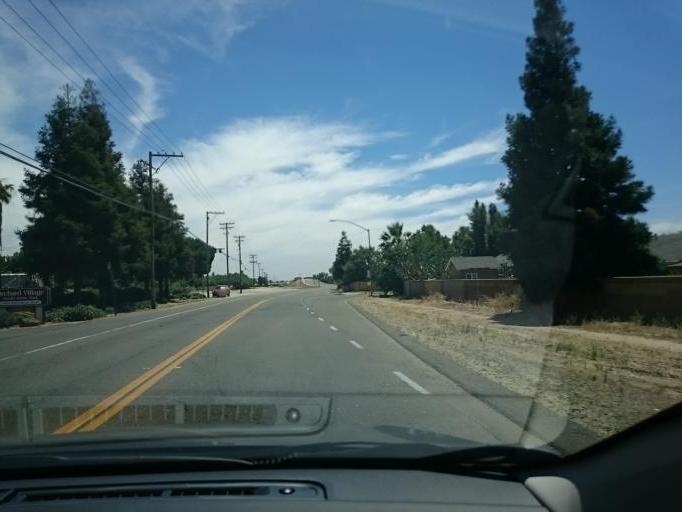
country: US
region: California
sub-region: Stanislaus County
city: Keyes
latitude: 37.5665
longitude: -120.9204
